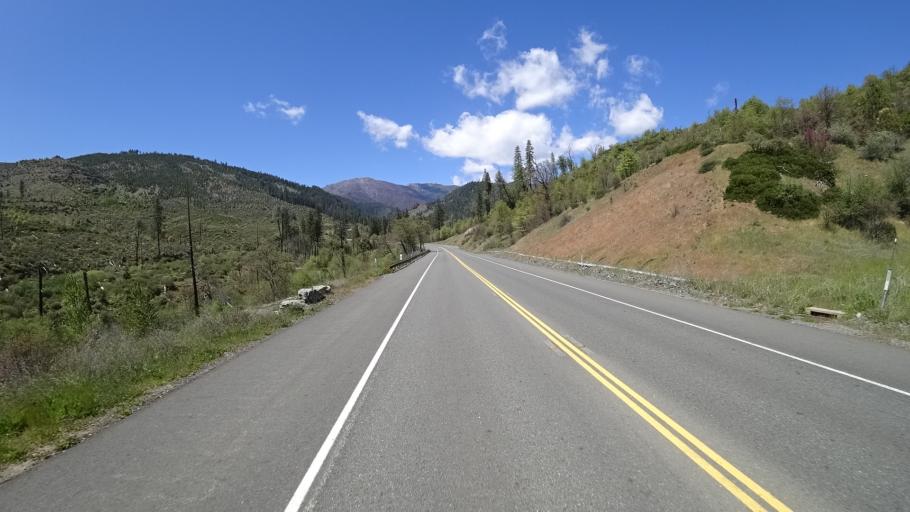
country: US
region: California
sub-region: Trinity County
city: Weaverville
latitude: 40.7400
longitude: -122.9671
